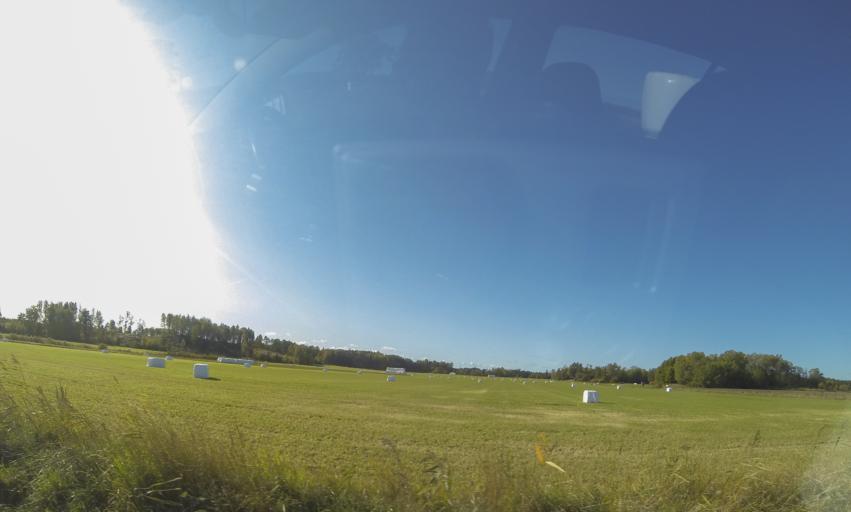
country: SE
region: Soedermanland
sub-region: Eskilstuna Kommun
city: Kvicksund
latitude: 59.5031
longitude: 16.3532
